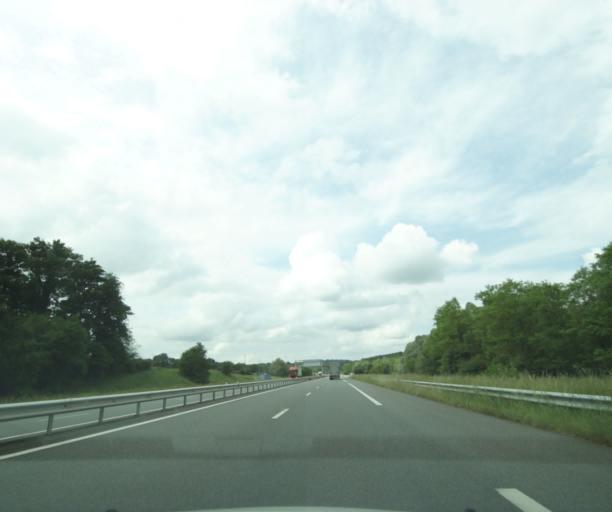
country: FR
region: Centre
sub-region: Departement du Cher
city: Orval
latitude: 46.7336
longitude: 2.4291
